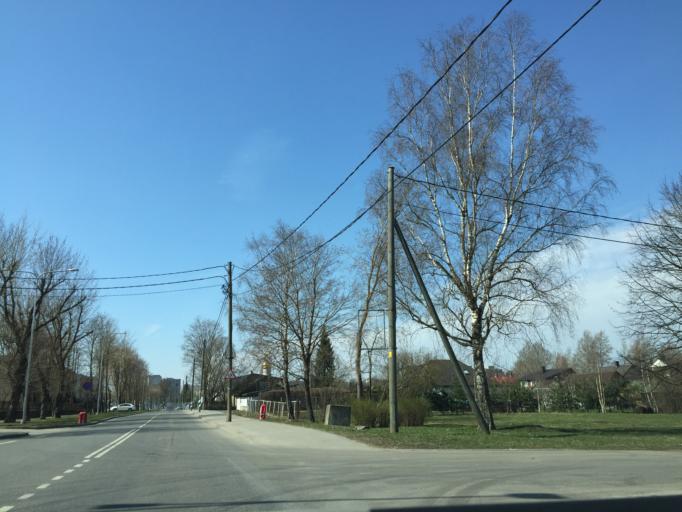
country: EE
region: Ida-Virumaa
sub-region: Narva linn
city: Narva
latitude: 59.3864
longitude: 28.1972
